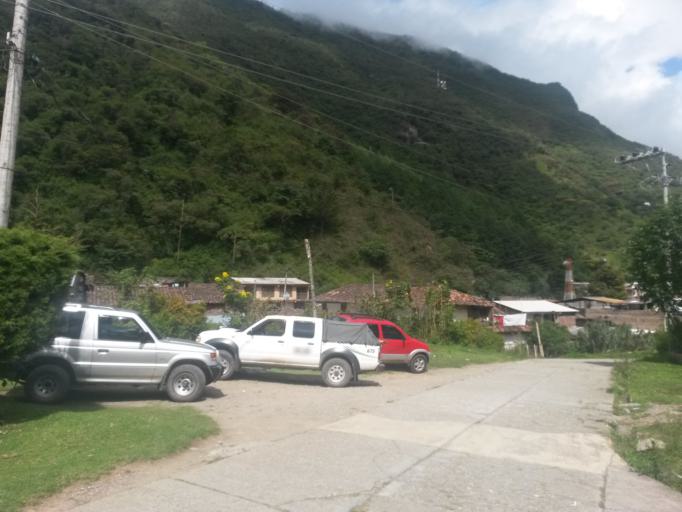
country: CO
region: Cauca
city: La Vega
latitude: 2.0006
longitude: -76.7762
